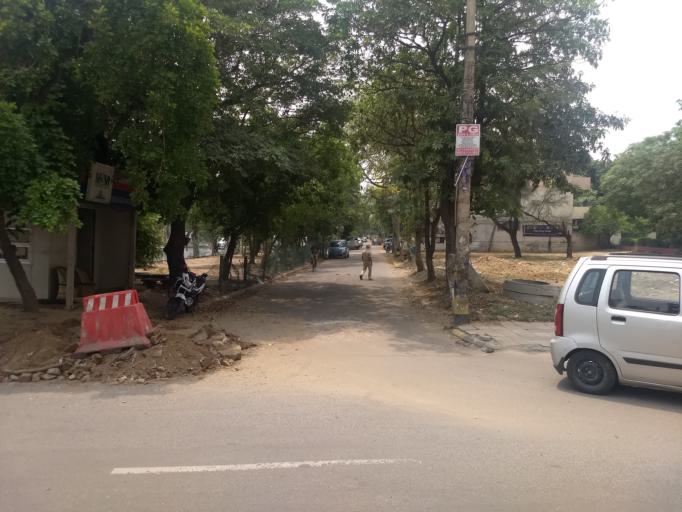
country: IN
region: Haryana
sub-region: Gurgaon
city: Gurgaon
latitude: 28.4619
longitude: 77.0870
